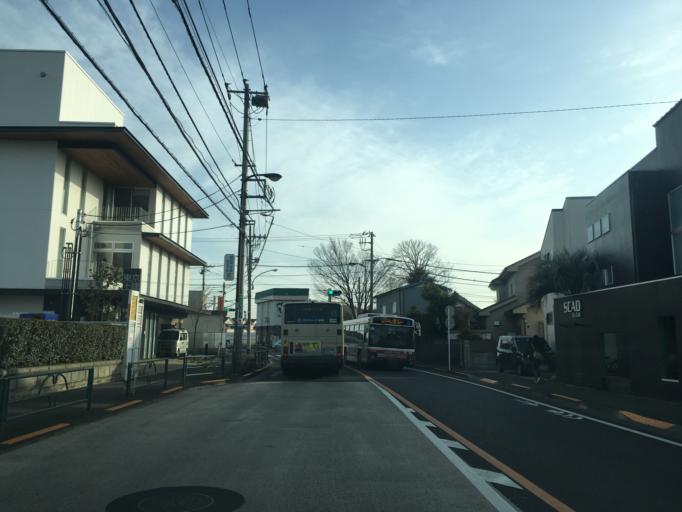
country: JP
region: Tokyo
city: Hino
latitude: 35.7105
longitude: 139.4273
